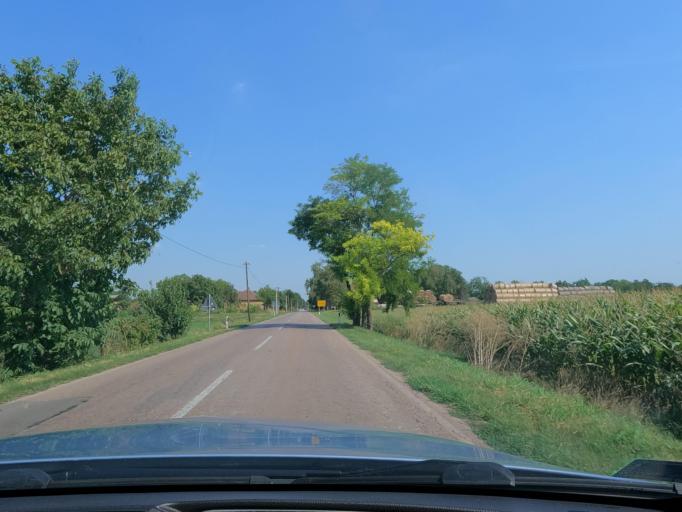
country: RS
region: Autonomna Pokrajina Vojvodina
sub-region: Severnobacki Okrug
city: Mali Igos
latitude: 45.7644
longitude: 19.7447
